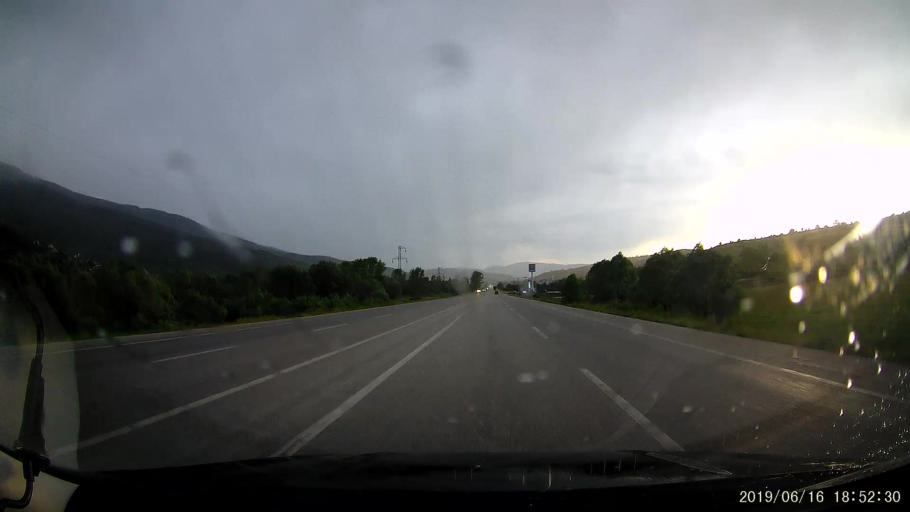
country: TR
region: Erzincan
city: Catalcam
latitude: 39.9024
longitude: 38.8998
